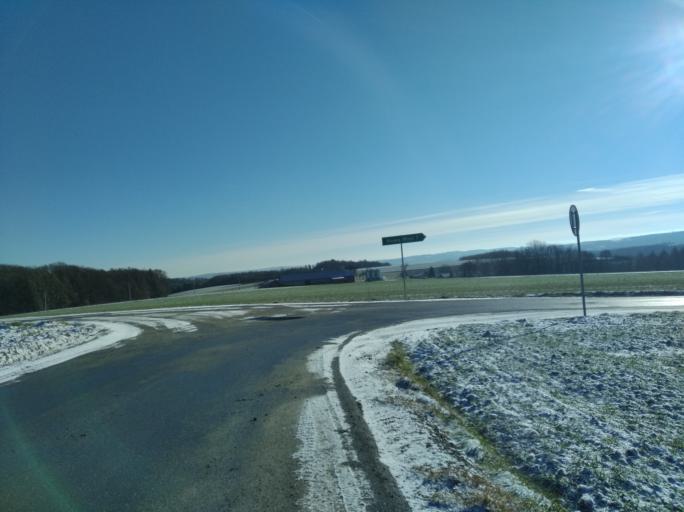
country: PL
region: Subcarpathian Voivodeship
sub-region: Powiat ropczycko-sedziszowski
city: Iwierzyce
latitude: 49.9710
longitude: 21.7567
